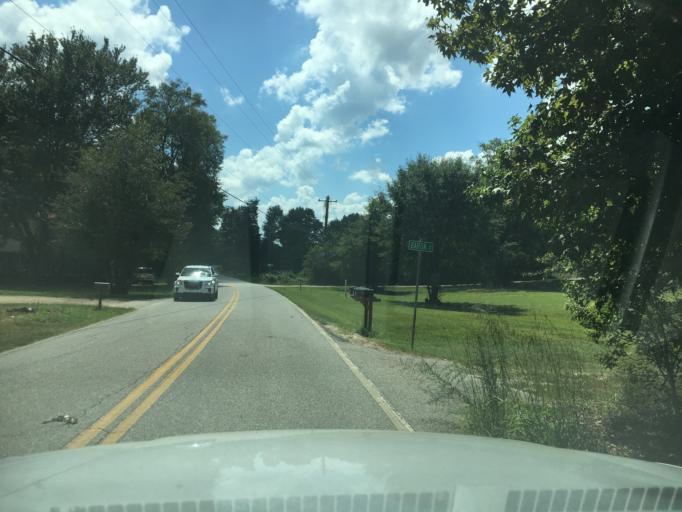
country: US
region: South Carolina
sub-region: Spartanburg County
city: Fairforest
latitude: 34.9079
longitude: -82.0512
